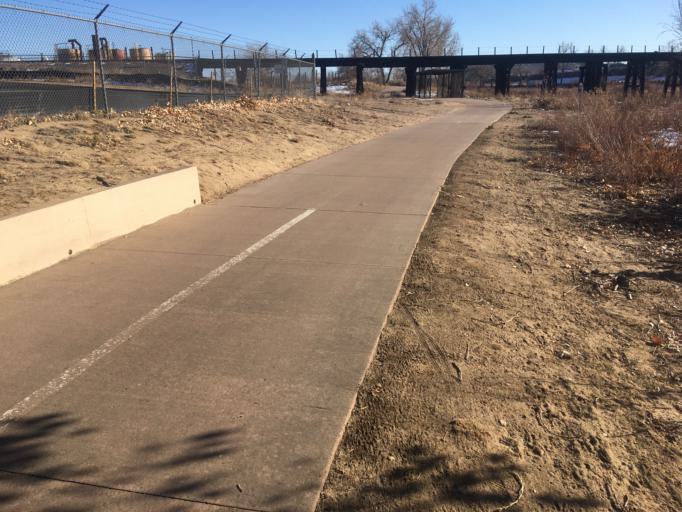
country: US
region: Colorado
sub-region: Adams County
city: Commerce City
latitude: 39.8013
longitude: -104.9388
